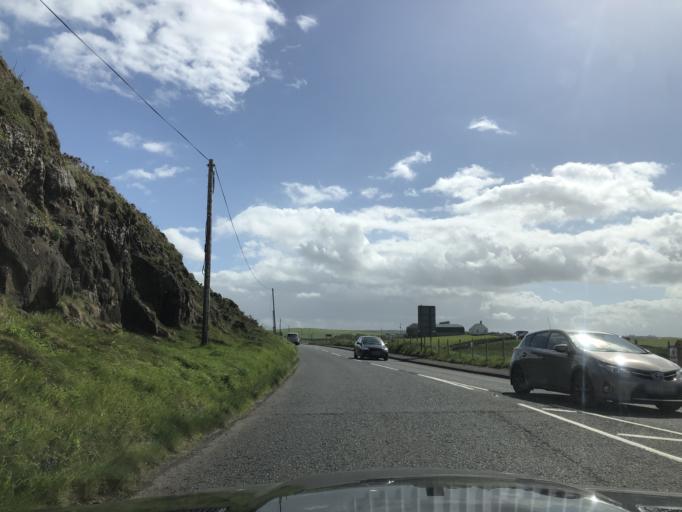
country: GB
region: Northern Ireland
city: Bushmills
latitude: 55.2120
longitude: -6.5753
